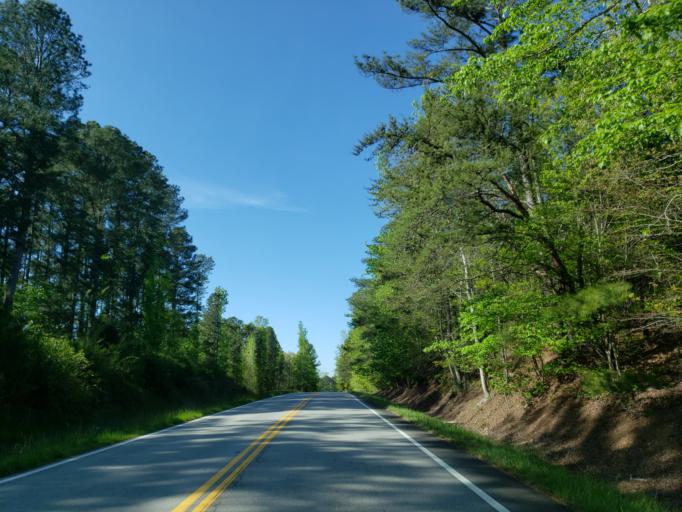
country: US
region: Georgia
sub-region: Haralson County
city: Tallapoosa
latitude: 33.8701
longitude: -85.3010
